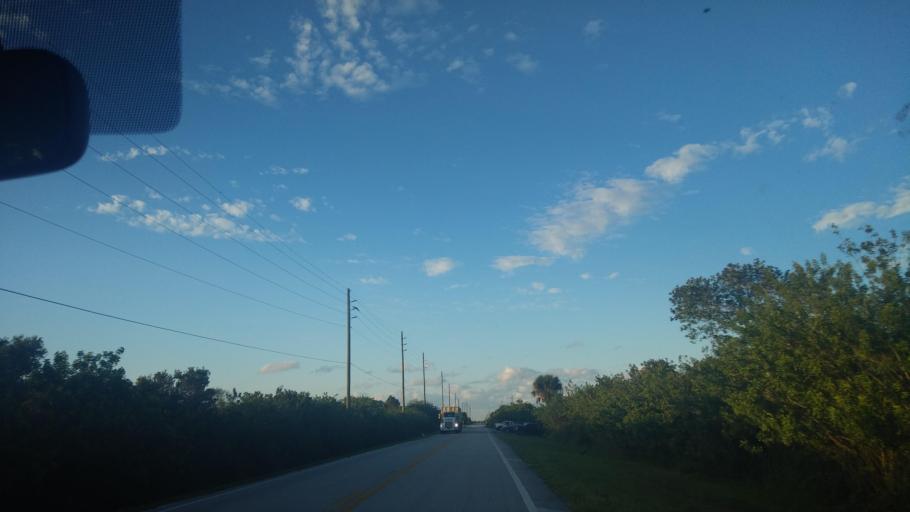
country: US
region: Florida
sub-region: Indian River County
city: Fellsmere
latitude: 27.6937
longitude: -80.6429
